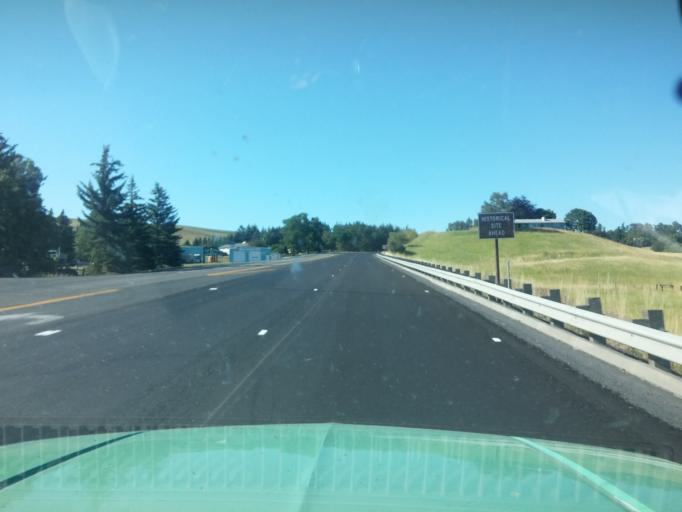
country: US
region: Idaho
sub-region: Latah County
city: Moscow
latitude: 46.6973
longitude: -117.0079
